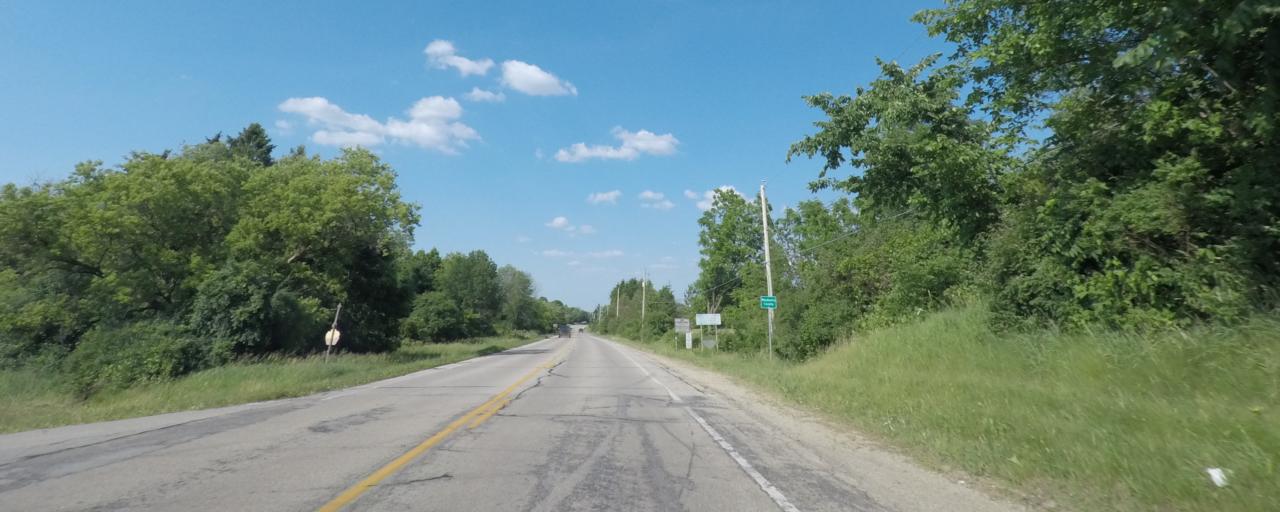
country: US
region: Wisconsin
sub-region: Waukesha County
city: Mukwonago
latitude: 42.8420
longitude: -88.2675
